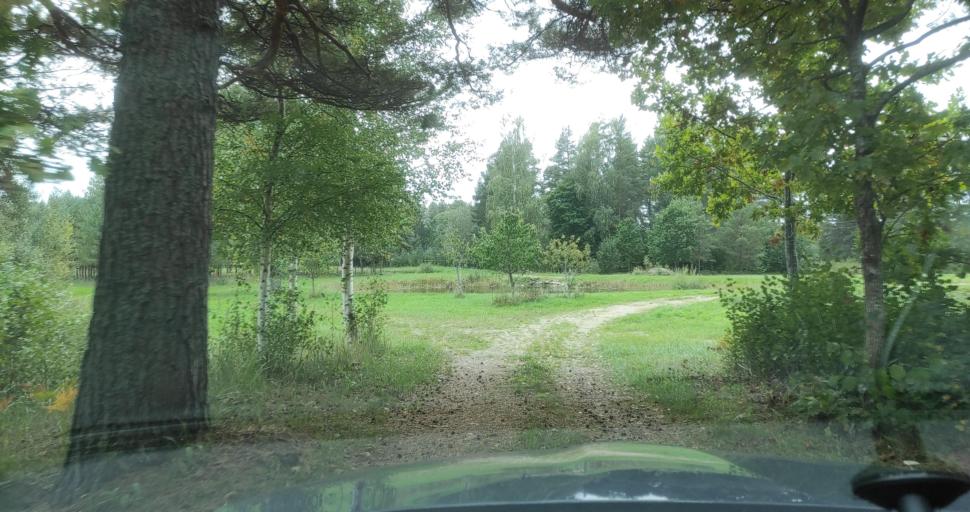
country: LV
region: Talsu Rajons
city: Stende
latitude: 57.0733
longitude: 22.3008
